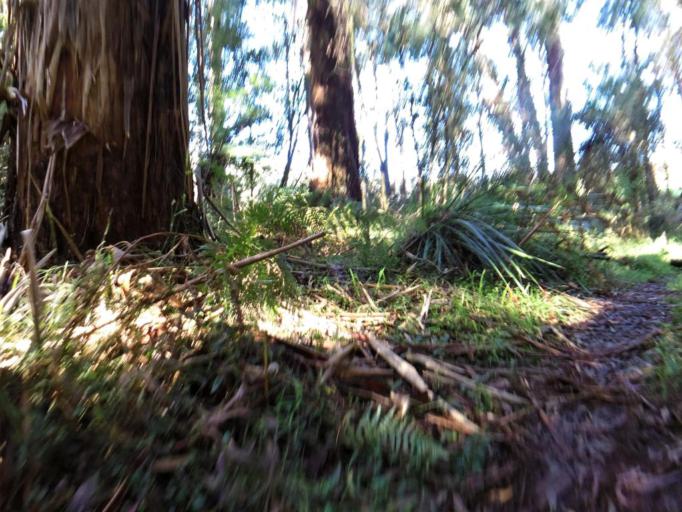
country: AU
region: Victoria
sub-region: Cardinia
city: Emerald
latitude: -37.9108
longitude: 145.4397
